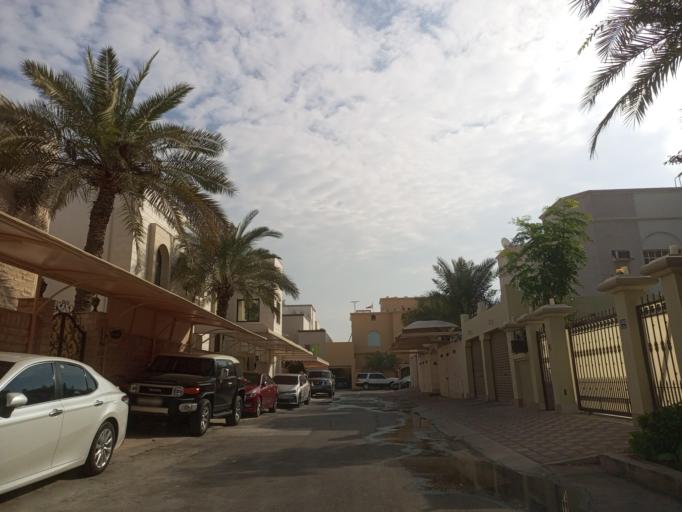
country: BH
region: Muharraq
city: Al Hadd
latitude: 26.2502
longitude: 50.6426
